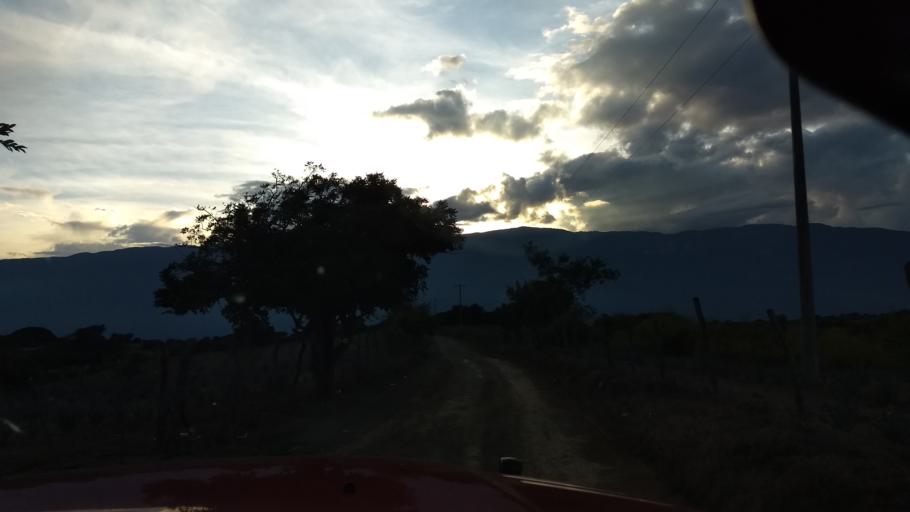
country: MX
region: Colima
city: Suchitlan
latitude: 19.4904
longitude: -103.7882
